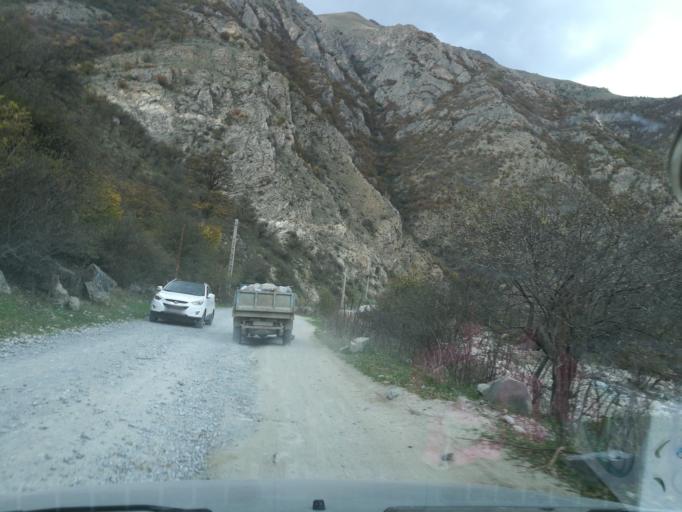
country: IR
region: Mazandaran
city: `Abbasabad
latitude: 36.4444
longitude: 51.0634
